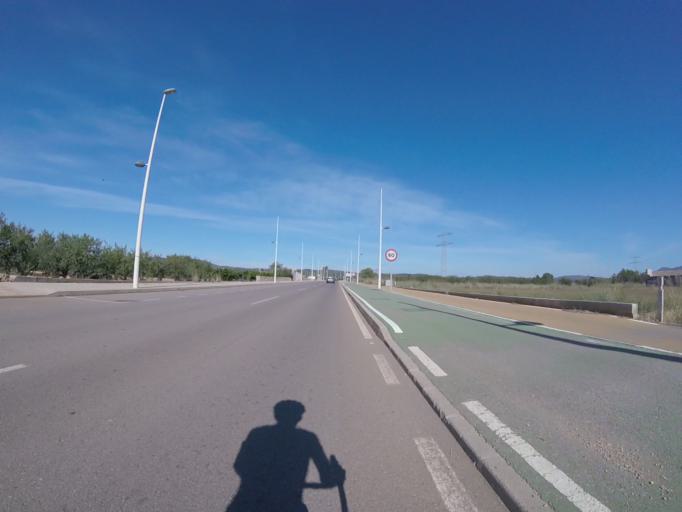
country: ES
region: Valencia
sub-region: Provincia de Castello
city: Torreblanca
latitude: 40.2157
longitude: 0.2211
